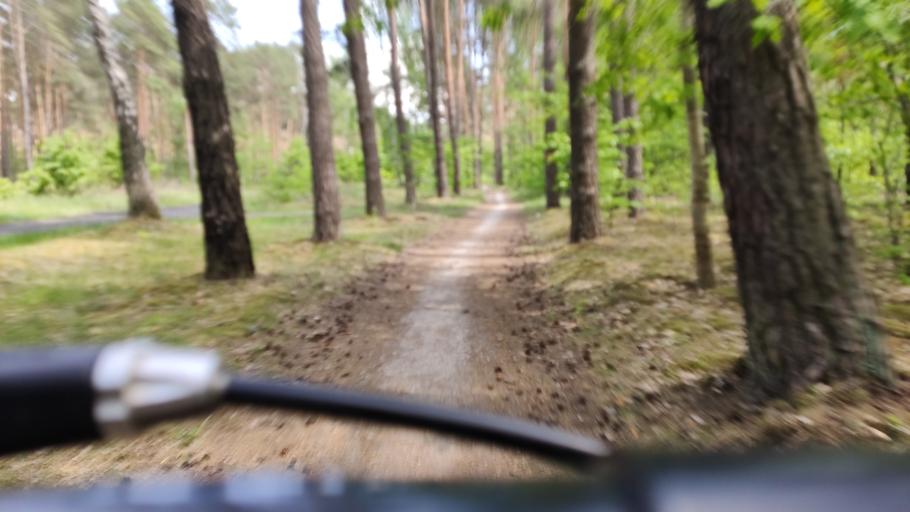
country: PL
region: Kujawsko-Pomorskie
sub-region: Wloclawek
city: Wloclawek
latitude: 52.6363
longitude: 19.1164
